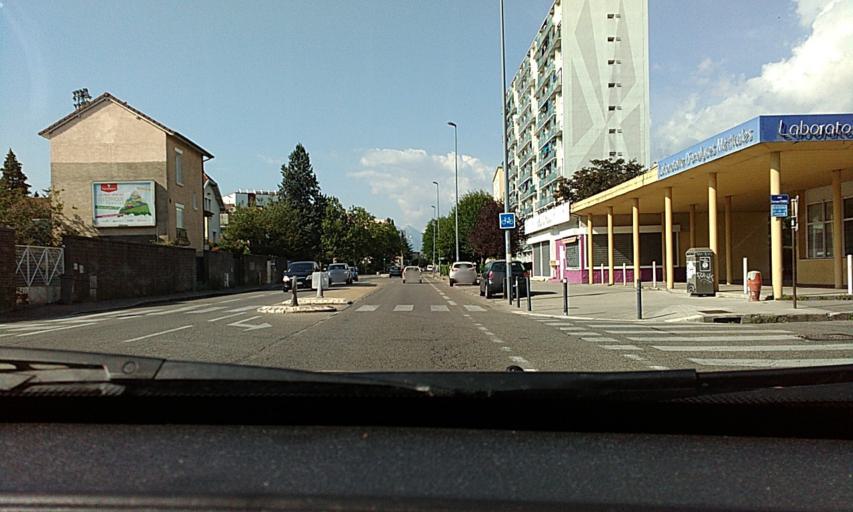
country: FR
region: Rhone-Alpes
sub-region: Departement de l'Isere
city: Grenoble
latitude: 45.1711
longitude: 5.7238
